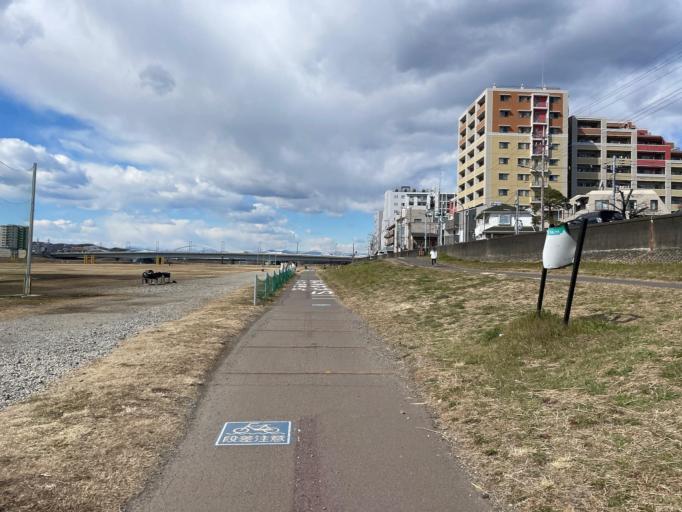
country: JP
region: Tokyo
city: Chofugaoka
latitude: 35.6427
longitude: 139.5308
